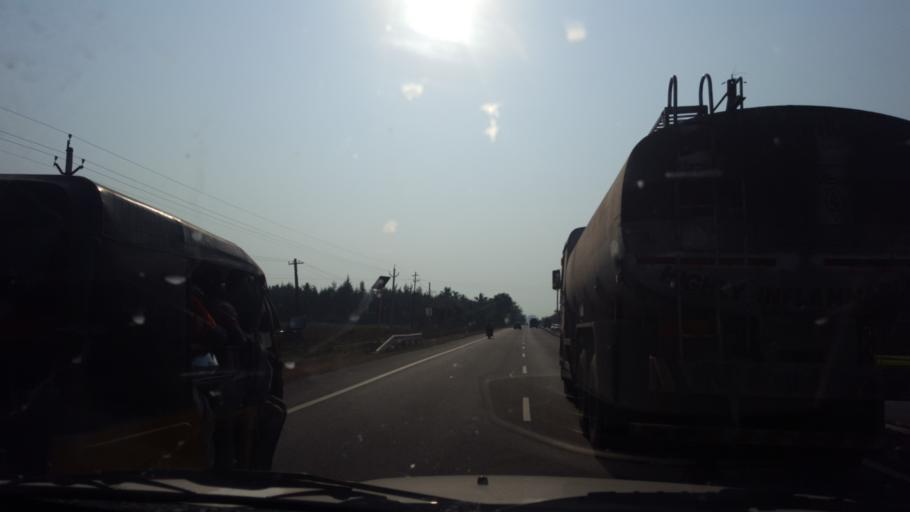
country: IN
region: Andhra Pradesh
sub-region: Vishakhapatnam
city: Etikoppaka
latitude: 17.4040
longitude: 82.6970
